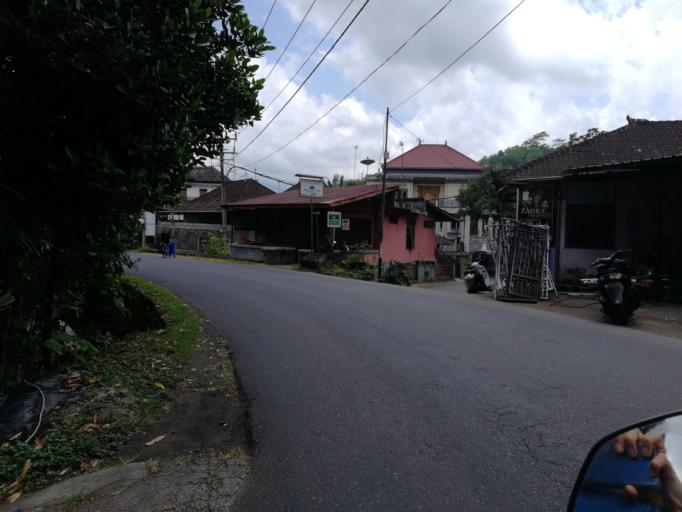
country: ID
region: Bali
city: Banjar Wangsian
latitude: -8.4585
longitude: 115.4500
